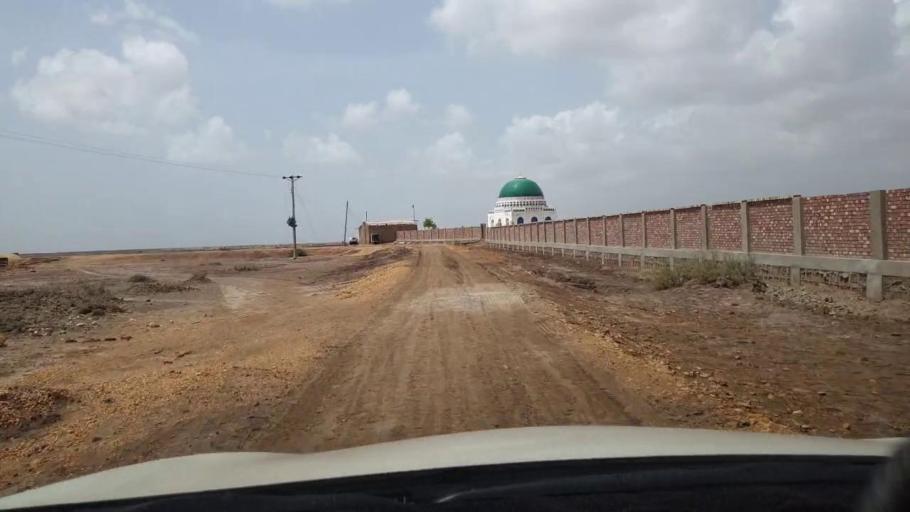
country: PK
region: Sindh
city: Kadhan
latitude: 24.3604
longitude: 68.8466
